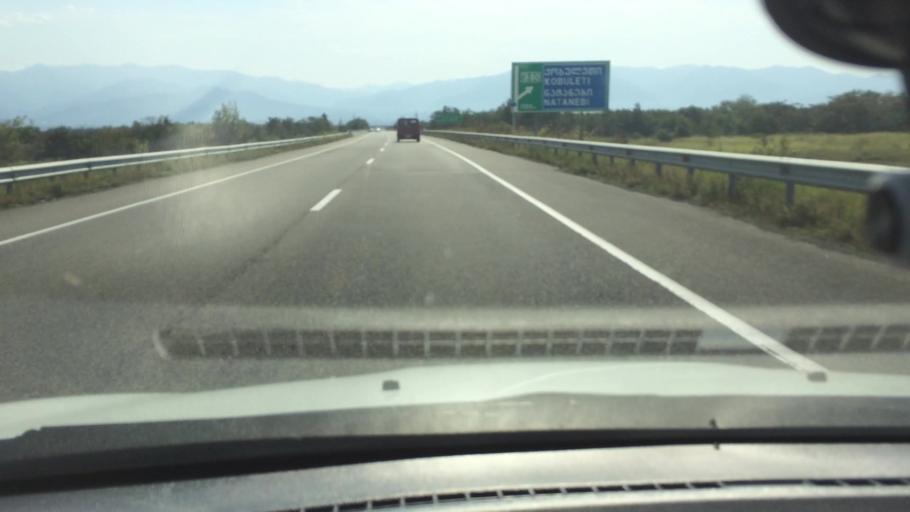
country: GE
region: Guria
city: Urek'i
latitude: 41.9111
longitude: 41.7818
